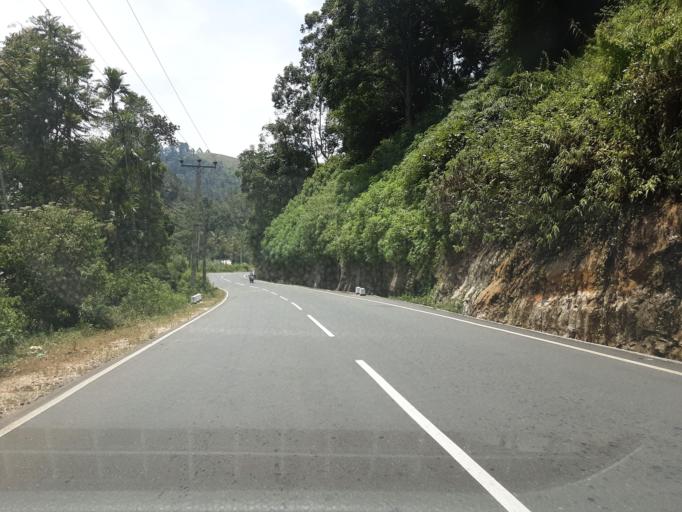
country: LK
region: Uva
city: Badulla
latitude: 6.9606
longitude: 80.9333
